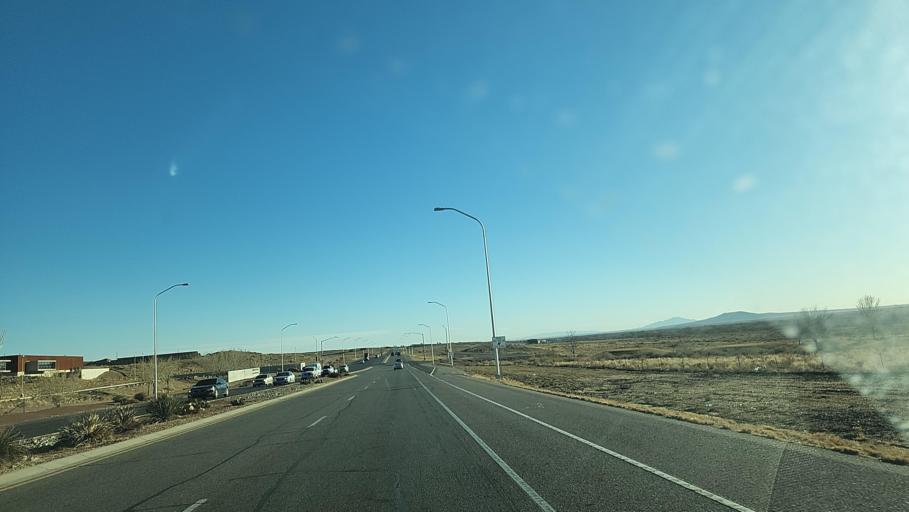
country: US
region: New Mexico
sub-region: Bernalillo County
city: South Valley
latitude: 34.9323
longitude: -106.6668
